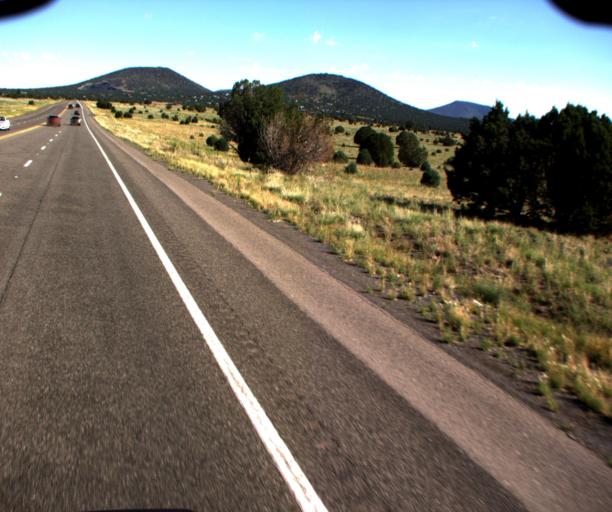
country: US
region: Arizona
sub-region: Coconino County
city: Williams
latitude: 35.3097
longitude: -112.1461
